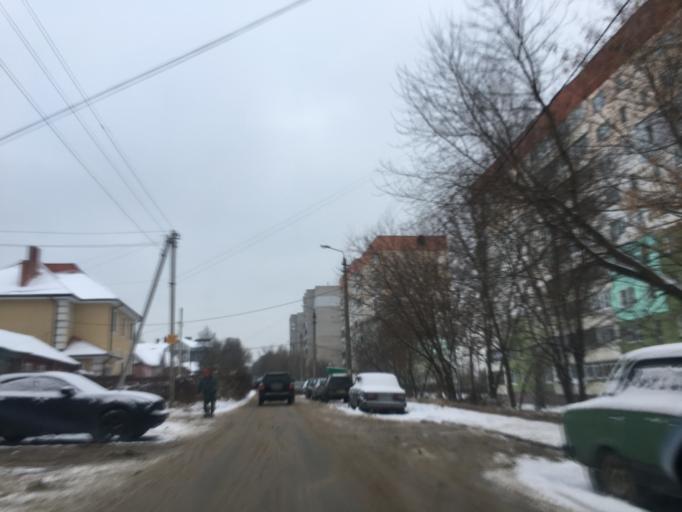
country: RU
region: Tula
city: Mendeleyevskiy
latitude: 54.1844
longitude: 37.5685
